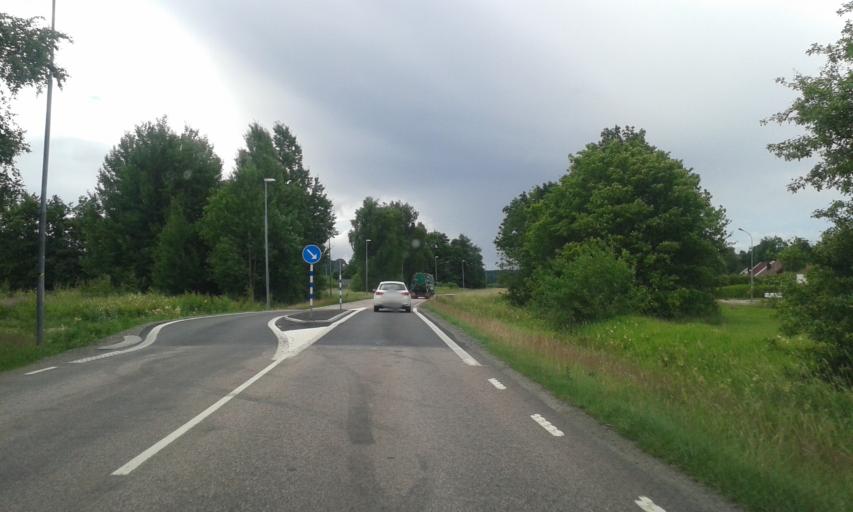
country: SE
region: Vaestra Goetaland
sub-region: Kungalvs Kommun
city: Diserod
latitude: 57.9228
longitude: 12.0311
